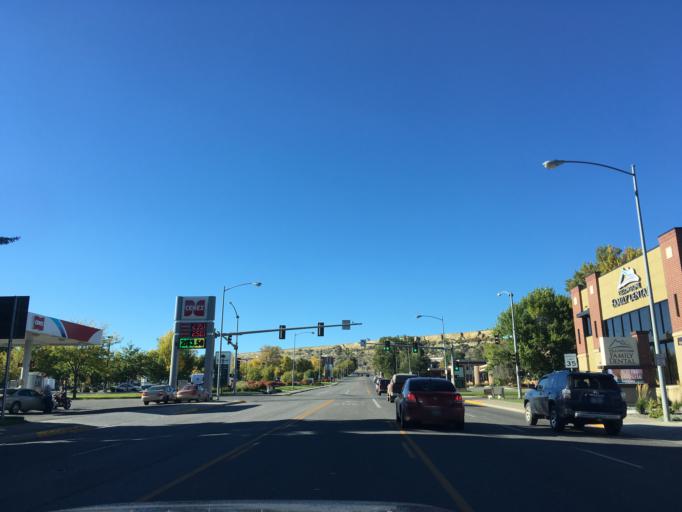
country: US
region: Montana
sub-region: Yellowstone County
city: Billings
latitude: 45.7921
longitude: -108.5138
